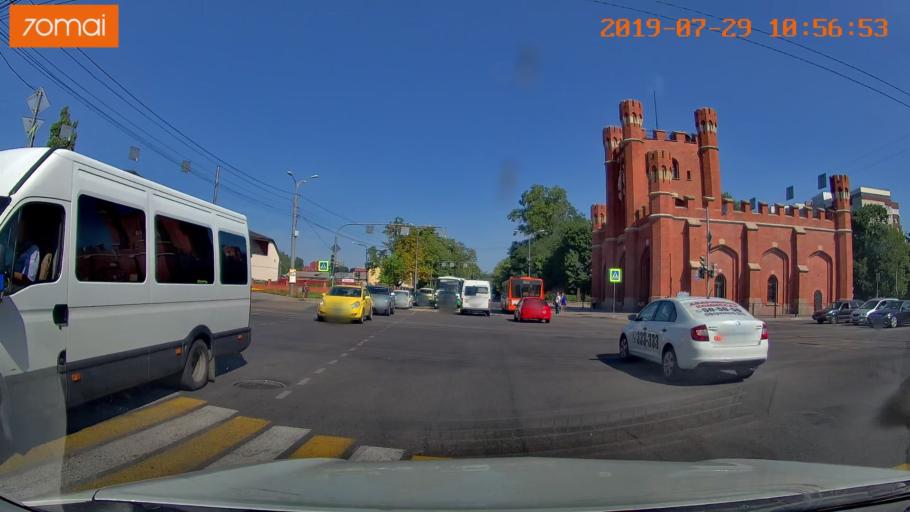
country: RU
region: Kaliningrad
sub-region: Gorod Kaliningrad
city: Kaliningrad
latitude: 54.7131
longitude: 20.5360
